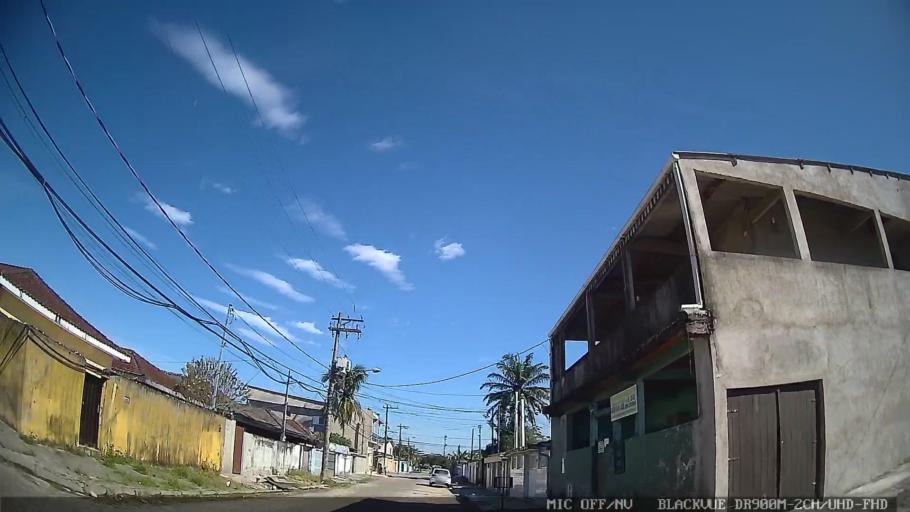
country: BR
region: Sao Paulo
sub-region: Santos
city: Santos
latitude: -23.9403
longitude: -46.2951
